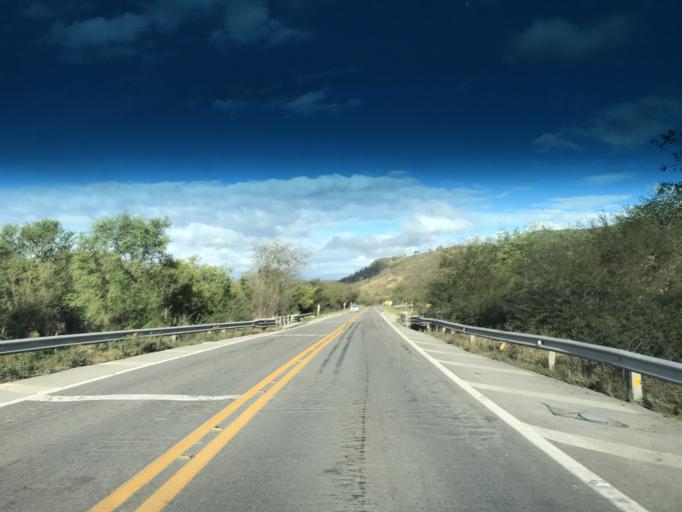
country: BR
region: Bahia
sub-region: Itaberaba
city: Itaberaba
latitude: -12.5010
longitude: -40.4271
